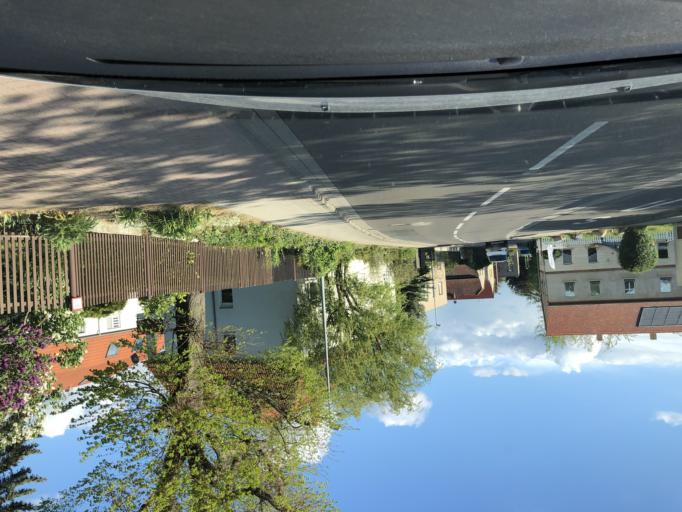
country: DE
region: Saxony
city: Bohlen
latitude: 51.2377
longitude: 12.3851
